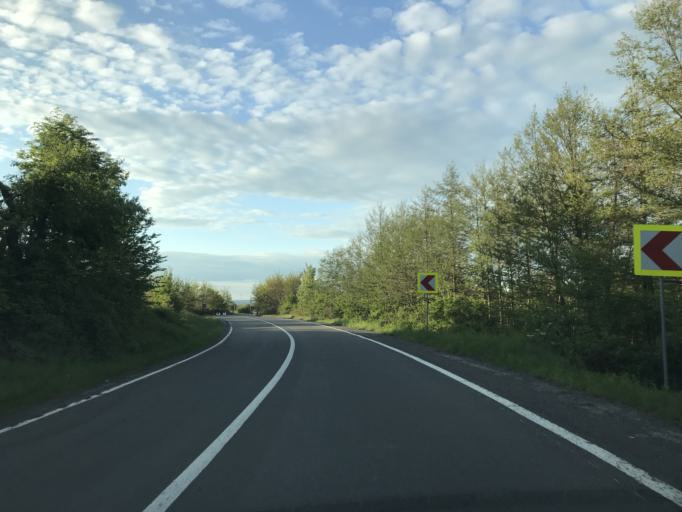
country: RO
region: Sibiu
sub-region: Comuna Cartisoara
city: Cartisoara
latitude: 45.7015
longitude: 24.5710
